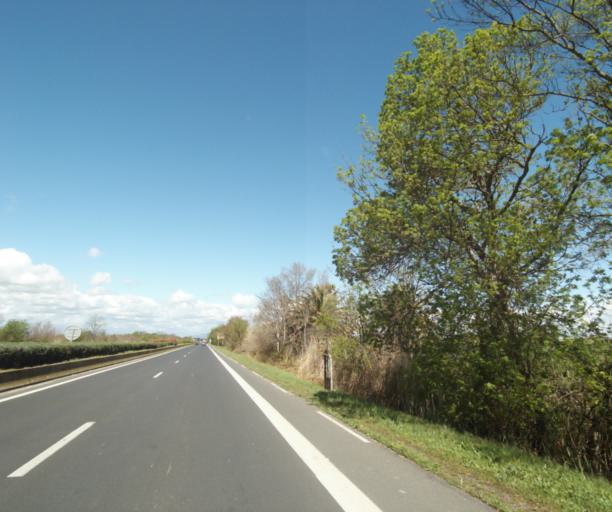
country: FR
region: Languedoc-Roussillon
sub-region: Departement de l'Herault
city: Lattes
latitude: 43.5439
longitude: 3.8963
